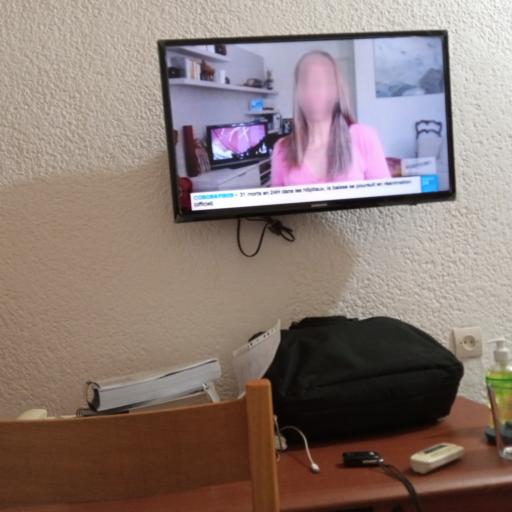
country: ML
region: Segou
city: Segou
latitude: 13.4490
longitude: -6.2673
